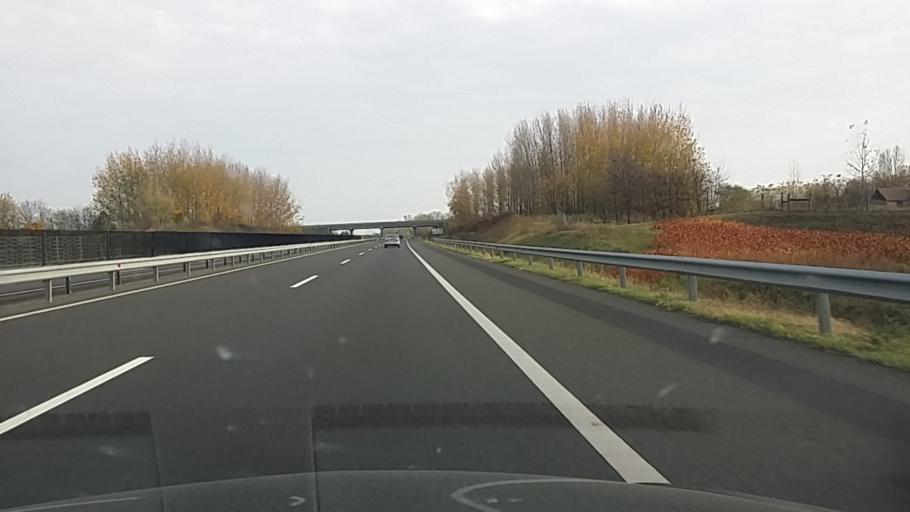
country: HU
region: Szabolcs-Szatmar-Bereg
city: Kalmanhaza
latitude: 47.9001
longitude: 21.5971
